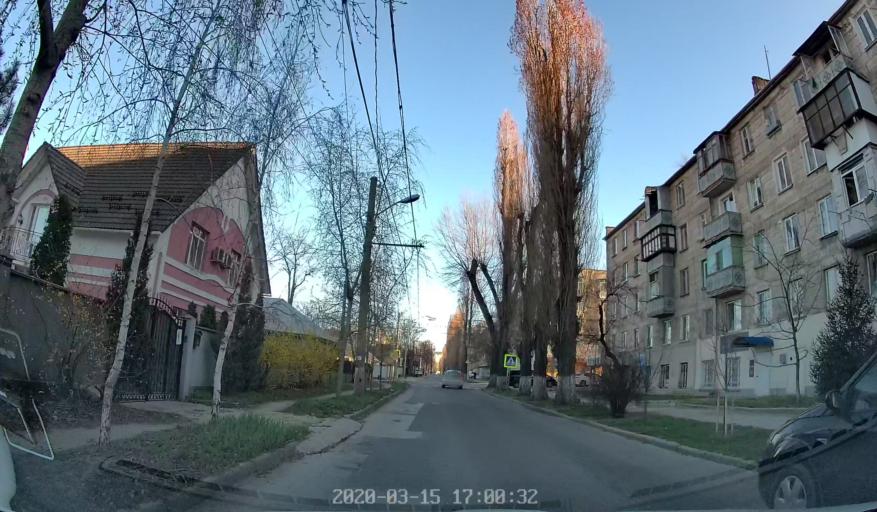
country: MD
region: Chisinau
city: Chisinau
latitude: 46.9947
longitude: 28.8672
